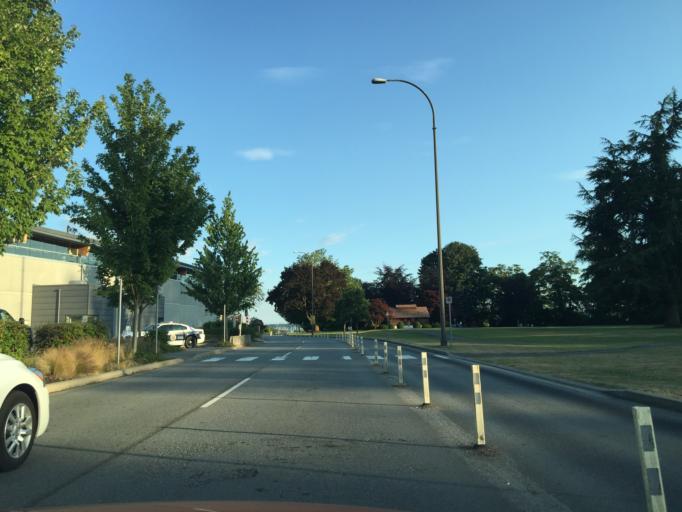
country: US
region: Washington
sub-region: Whatcom County
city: Blaine
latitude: 49.0056
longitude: -122.7579
